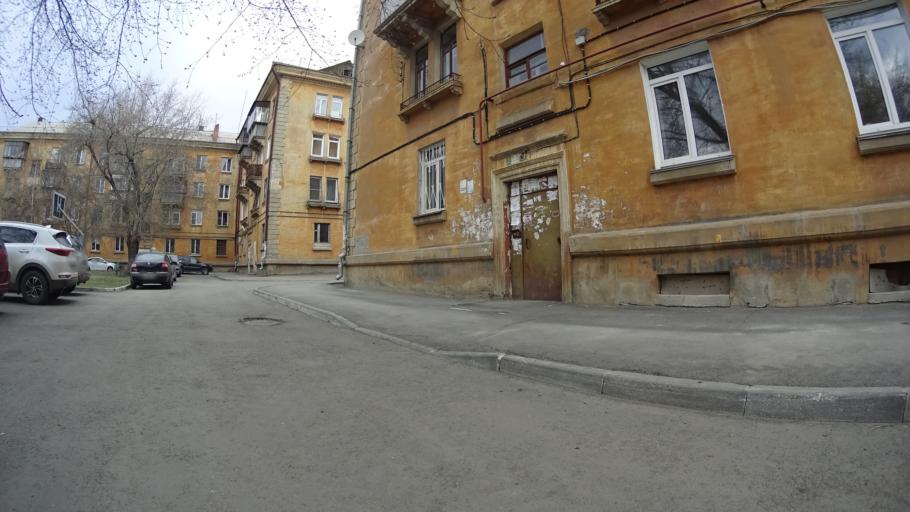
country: RU
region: Chelyabinsk
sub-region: Gorod Chelyabinsk
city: Chelyabinsk
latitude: 55.1637
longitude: 61.4410
